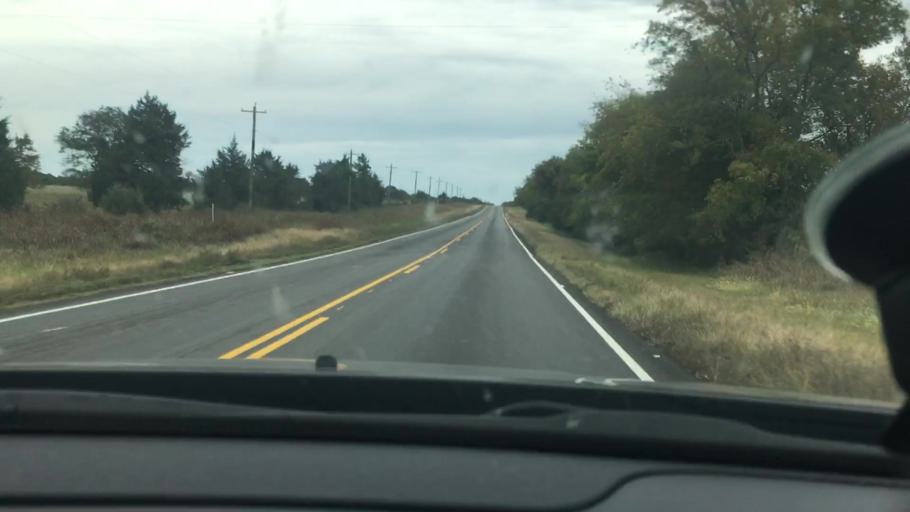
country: US
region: Oklahoma
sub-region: Coal County
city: Coalgate
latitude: 34.3926
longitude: -96.4245
